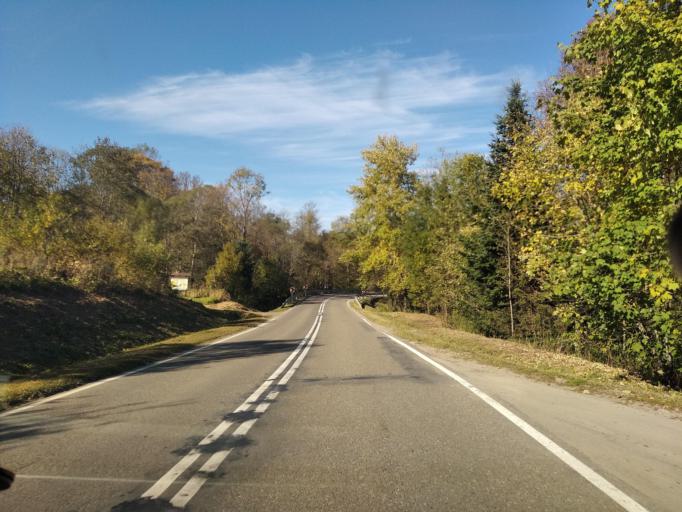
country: PL
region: Subcarpathian Voivodeship
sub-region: Powiat leski
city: Cisna
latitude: 49.2526
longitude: 22.2854
